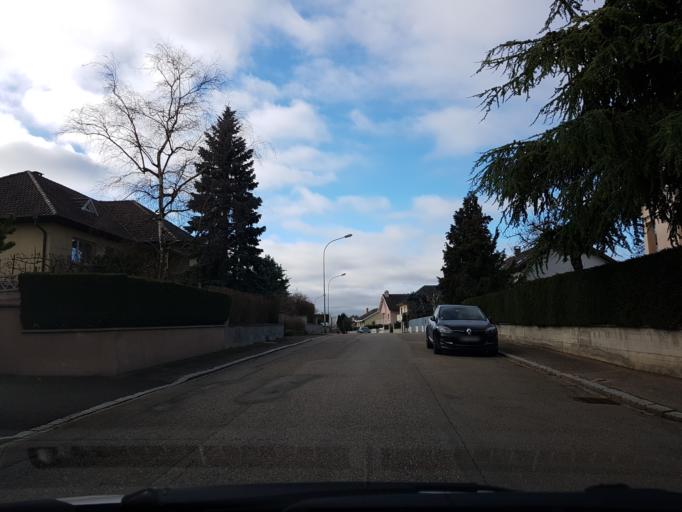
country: FR
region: Alsace
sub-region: Departement du Haut-Rhin
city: Riedisheim
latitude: 47.7531
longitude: 7.3767
